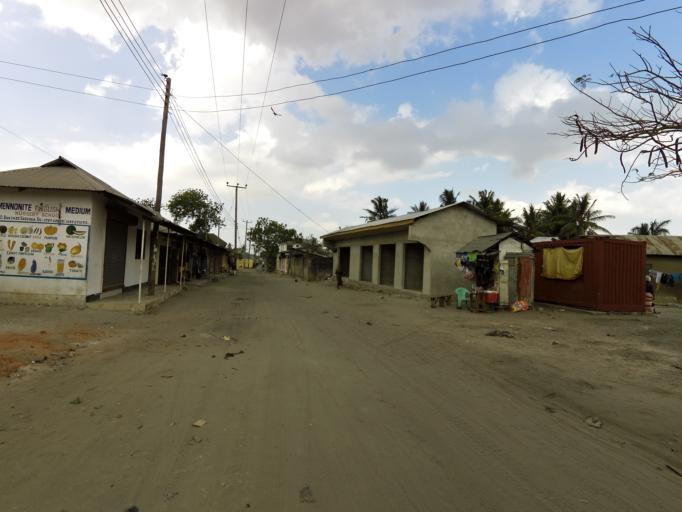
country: TZ
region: Dar es Salaam
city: Magomeni
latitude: -6.8440
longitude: 39.1910
